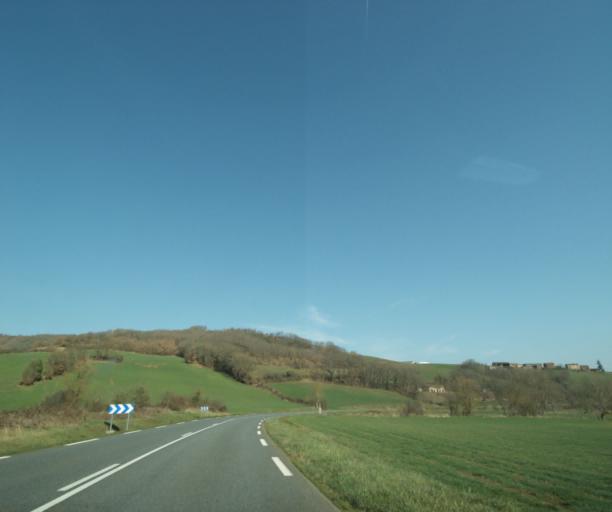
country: FR
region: Midi-Pyrenees
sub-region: Departement de l'Aveyron
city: Saint-Affrique
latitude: 43.9266
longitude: 2.8217
